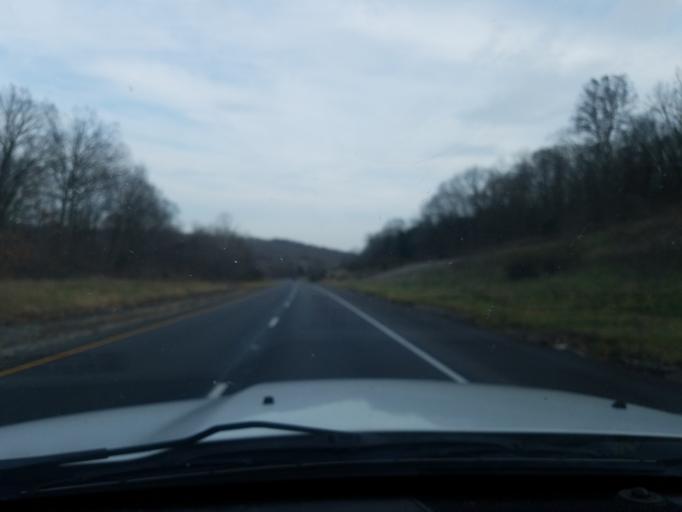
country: US
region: Indiana
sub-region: Crawford County
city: English
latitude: 38.2437
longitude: -86.4191
